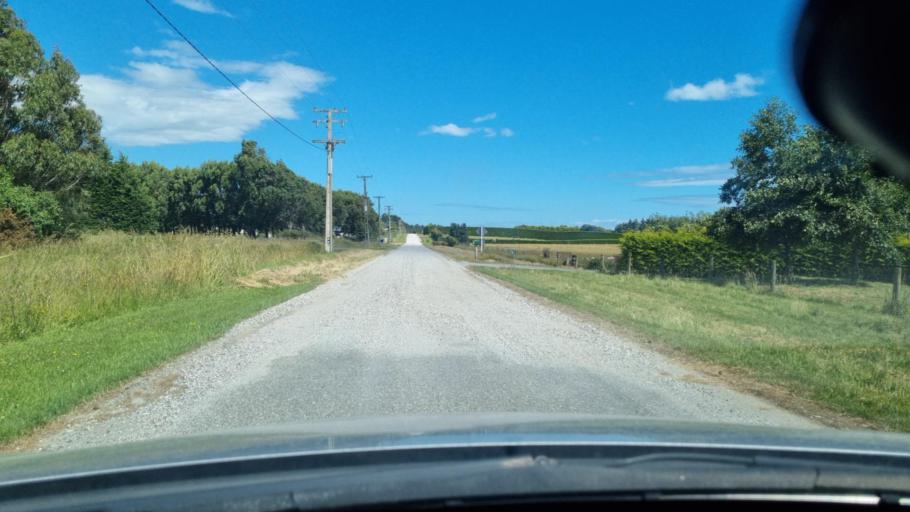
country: NZ
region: Southland
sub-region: Invercargill City
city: Invercargill
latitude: -46.4108
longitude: 168.4401
